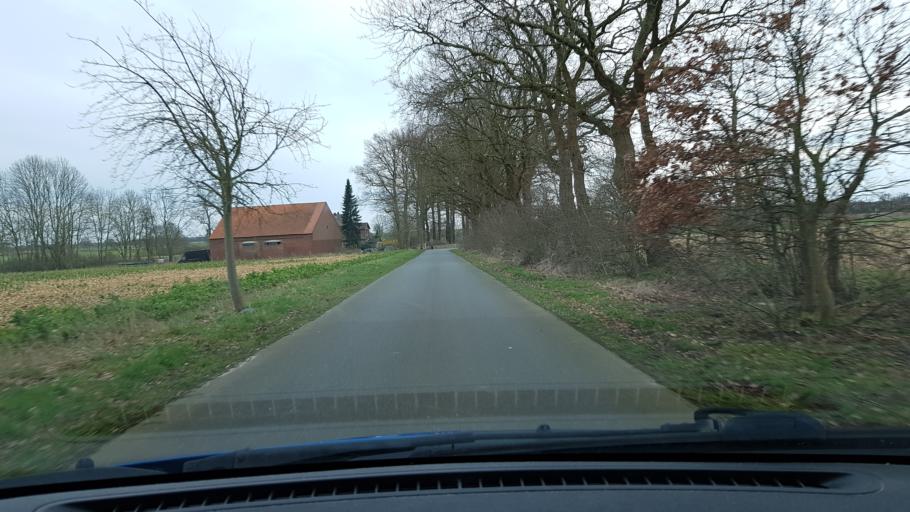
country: DE
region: Lower Saxony
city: Oetzen
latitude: 53.0069
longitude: 10.6535
